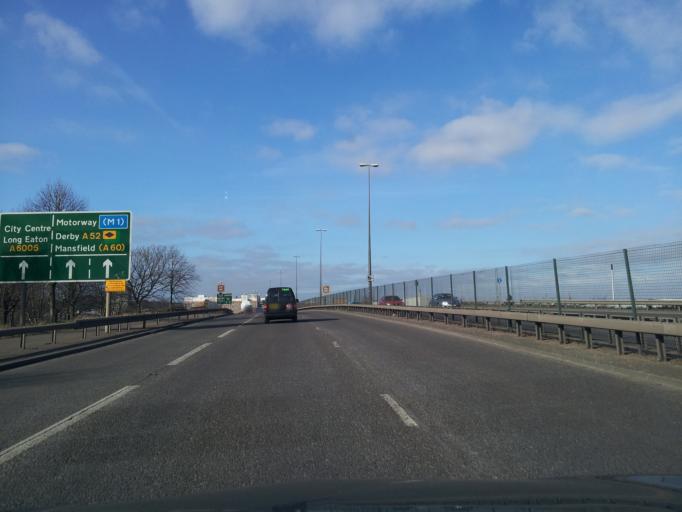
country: GB
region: England
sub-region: Nottingham
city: Nottingham
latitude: 52.9379
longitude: -1.1763
